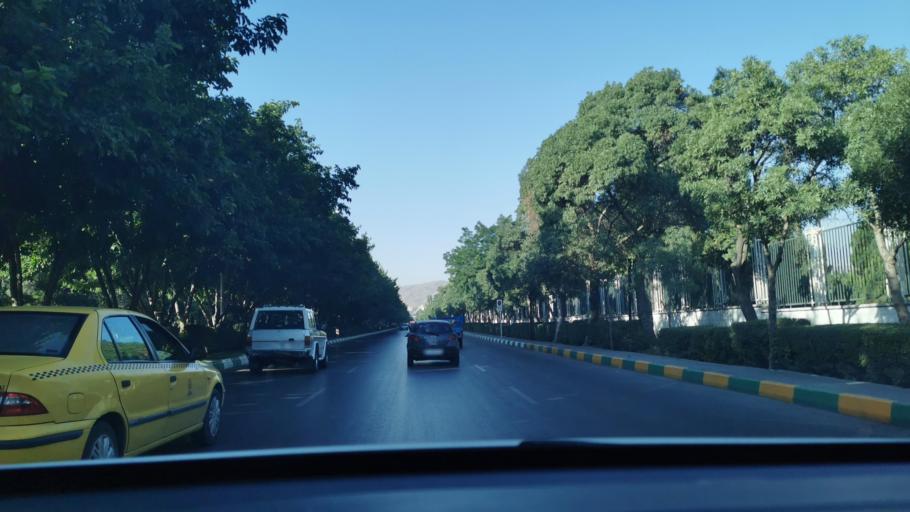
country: IR
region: Razavi Khorasan
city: Mashhad
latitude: 36.2982
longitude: 59.5621
